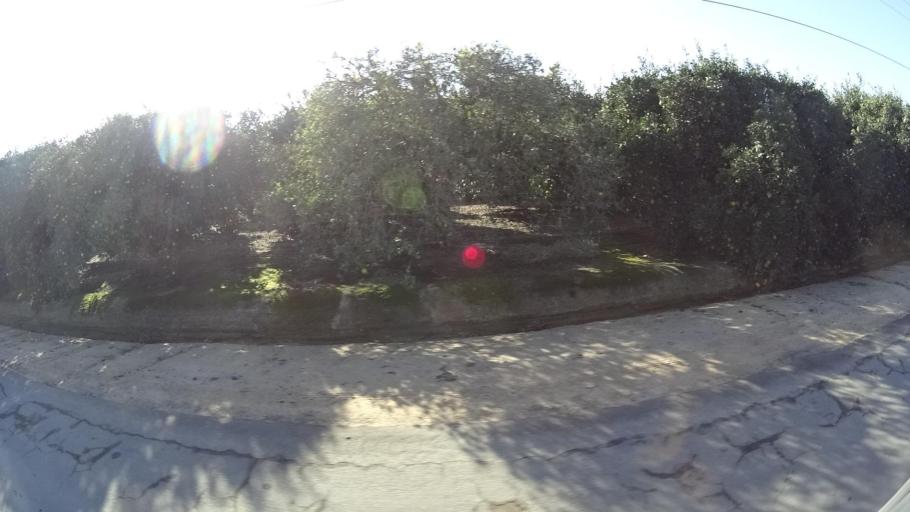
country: US
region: California
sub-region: Tulare County
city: Richgrove
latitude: 35.7326
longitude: -119.1370
